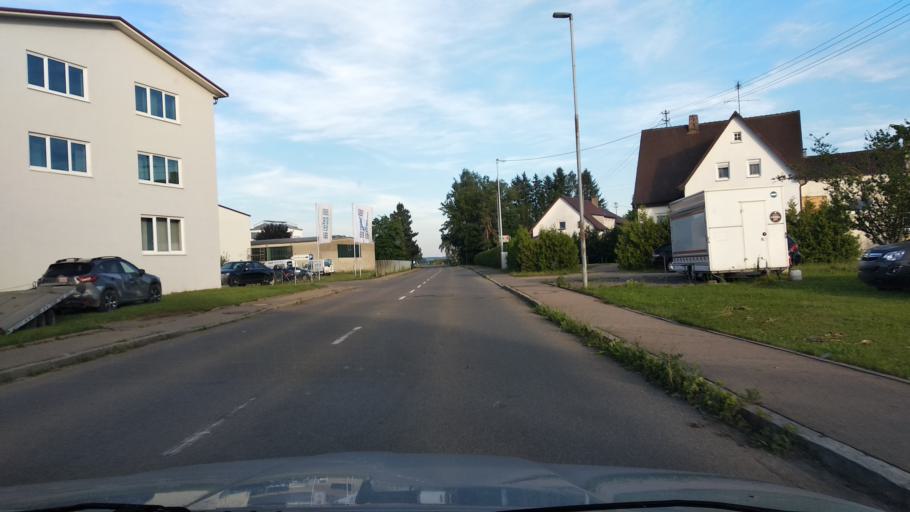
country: DE
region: Baden-Wuerttemberg
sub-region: Tuebingen Region
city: Kirchberg an der Iller
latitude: 48.1308
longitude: 10.0835
